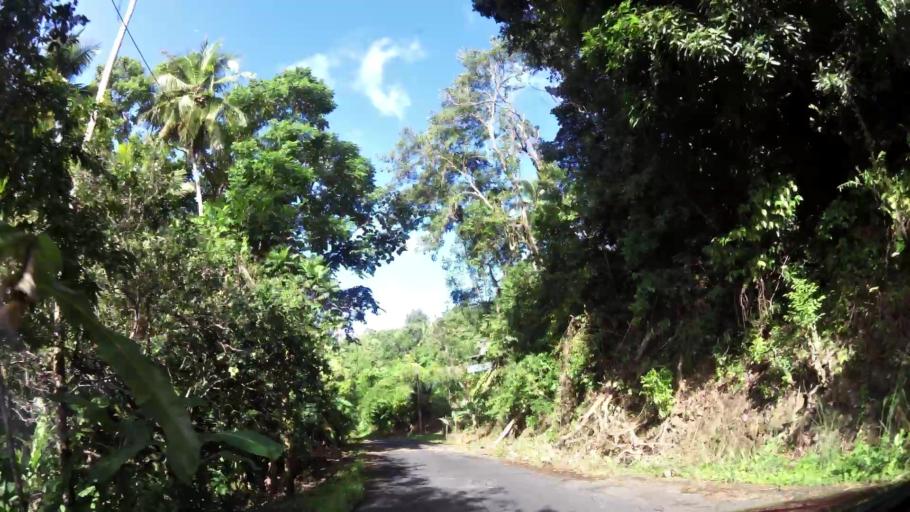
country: DM
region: Saint John
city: Portsmouth
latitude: 15.5749
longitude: -61.4352
